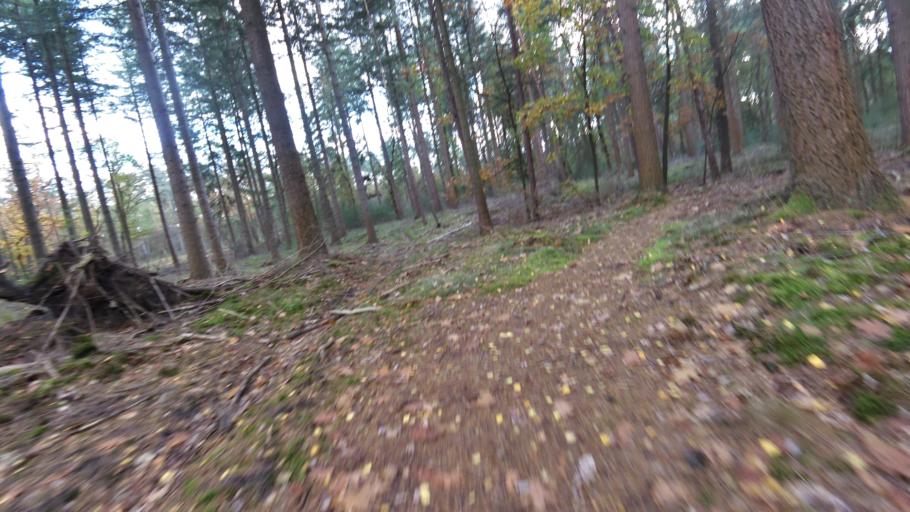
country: NL
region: Gelderland
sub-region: Gemeente Nunspeet
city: Nunspeet
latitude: 52.3527
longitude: 5.8309
